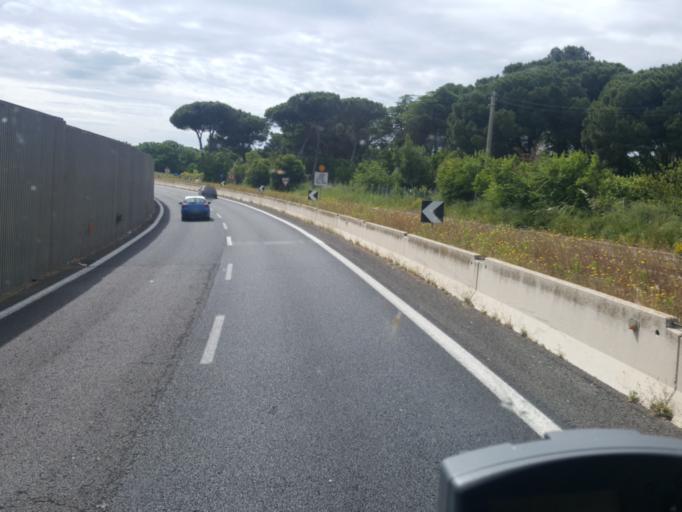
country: IT
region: Latium
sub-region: Citta metropolitana di Roma Capitale
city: Ara Nova
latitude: 41.9192
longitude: 12.2351
